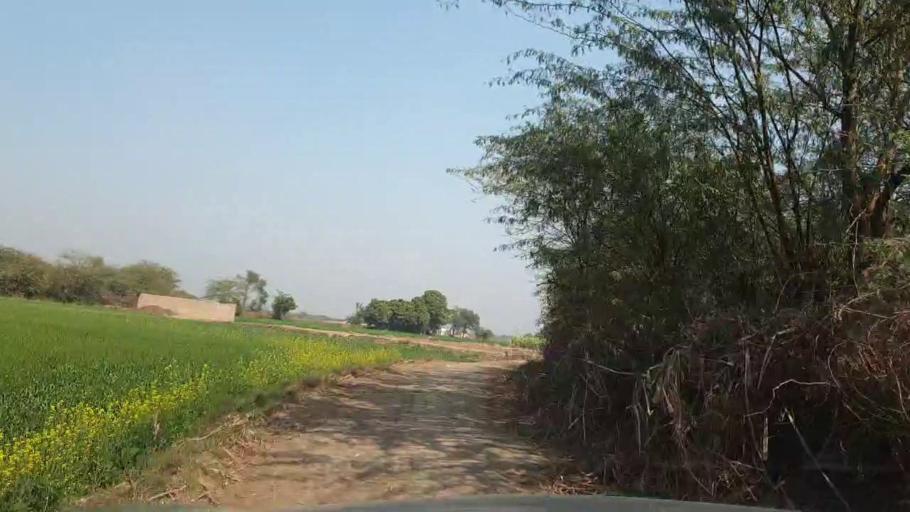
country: PK
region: Sindh
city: Tando Allahyar
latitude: 25.5538
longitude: 68.7245
